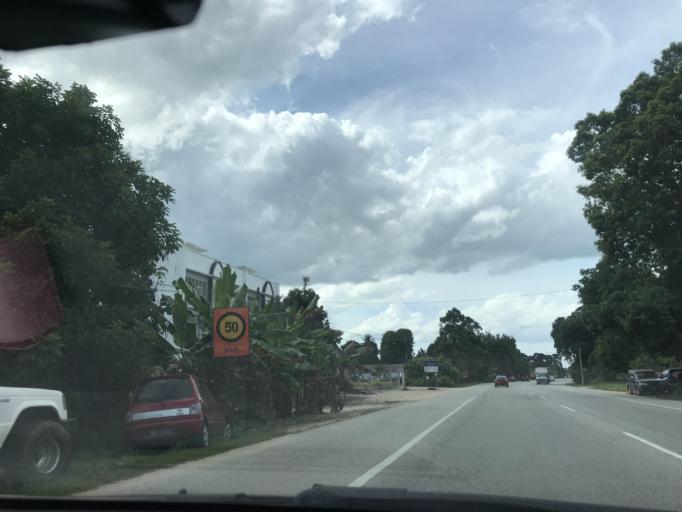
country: MY
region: Kelantan
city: Kampong Pangkal Kalong
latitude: 5.9160
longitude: 102.1881
